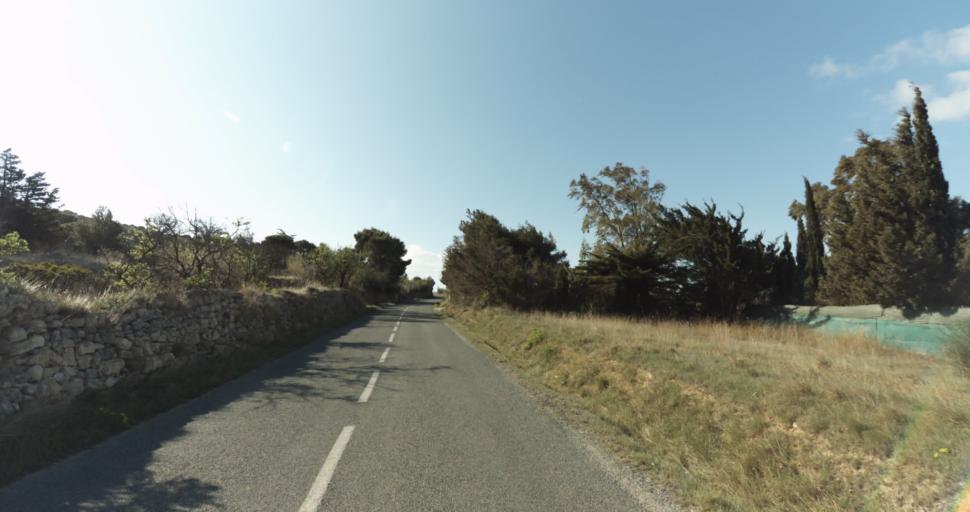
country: FR
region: Languedoc-Roussillon
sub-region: Departement de l'Aude
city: Leucate
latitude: 42.9248
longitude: 3.0142
